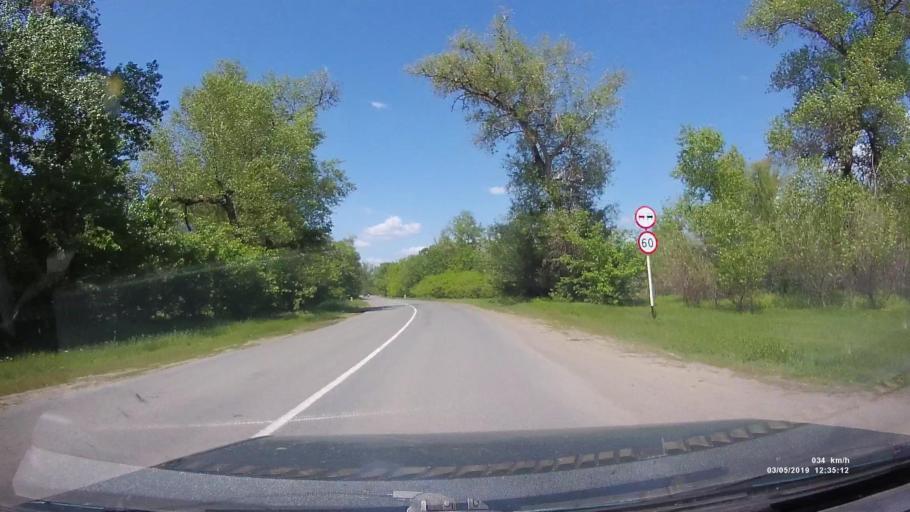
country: RU
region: Rostov
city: Semikarakorsk
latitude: 47.5250
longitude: 40.7623
